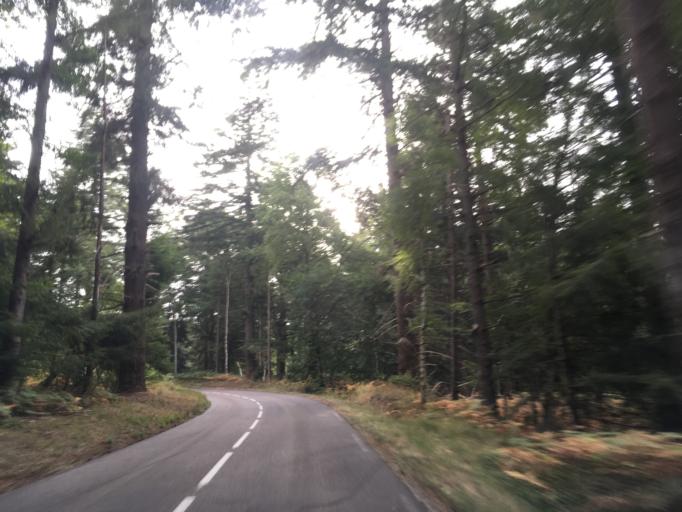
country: FR
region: Ile-de-France
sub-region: Departement des Yvelines
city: Limetz-Villez
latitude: 49.1029
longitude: 1.5166
